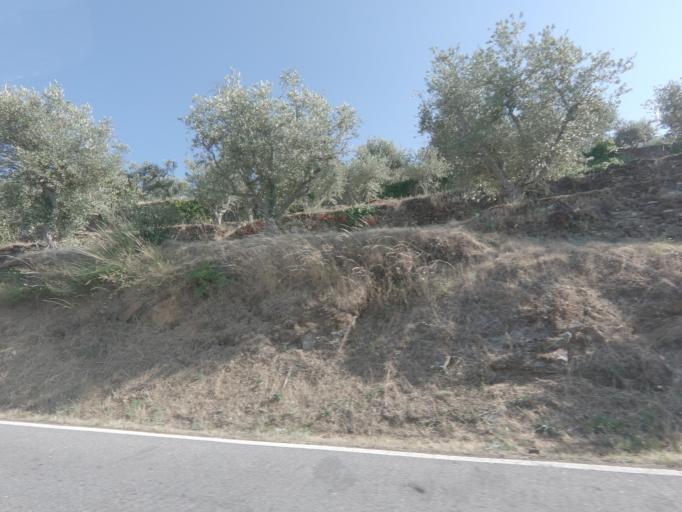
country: PT
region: Viseu
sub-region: Tabuaco
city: Tabuaco
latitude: 41.1202
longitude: -7.5652
